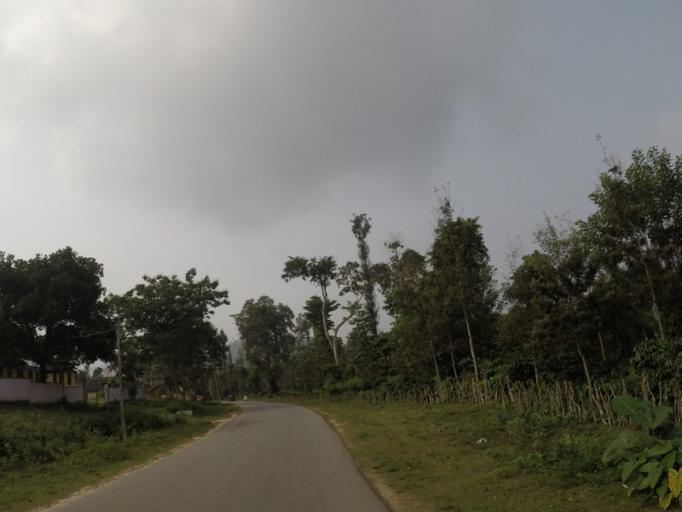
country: IN
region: Karnataka
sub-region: Chikmagalur
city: Mudigere
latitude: 13.2781
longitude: 75.4840
